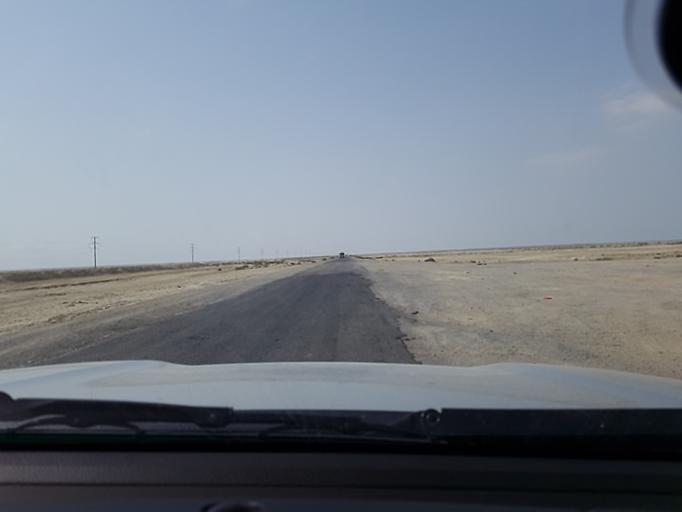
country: TM
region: Balkan
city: Gumdag
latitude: 38.9962
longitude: 54.5863
